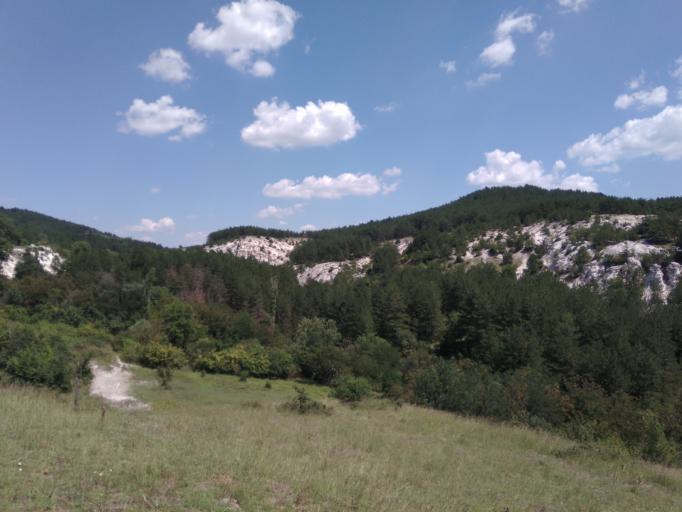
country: BG
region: Kurdzhali
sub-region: Obshtina Kurdzhali
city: Kurdzhali
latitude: 41.6561
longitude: 25.3996
